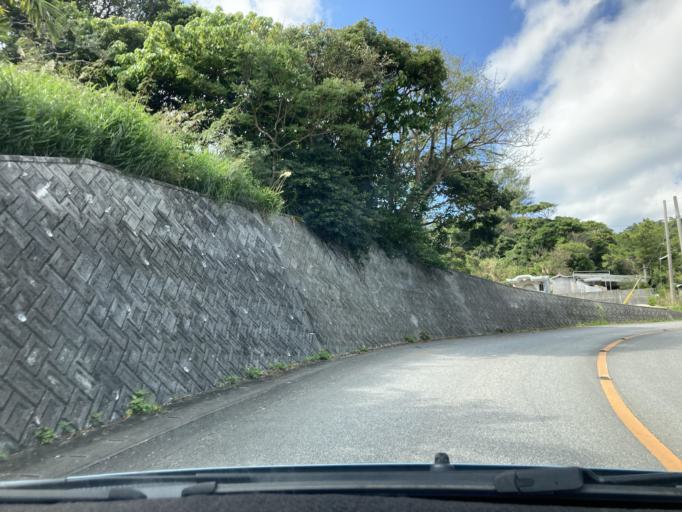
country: JP
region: Okinawa
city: Ginowan
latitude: 26.1816
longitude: 127.7662
